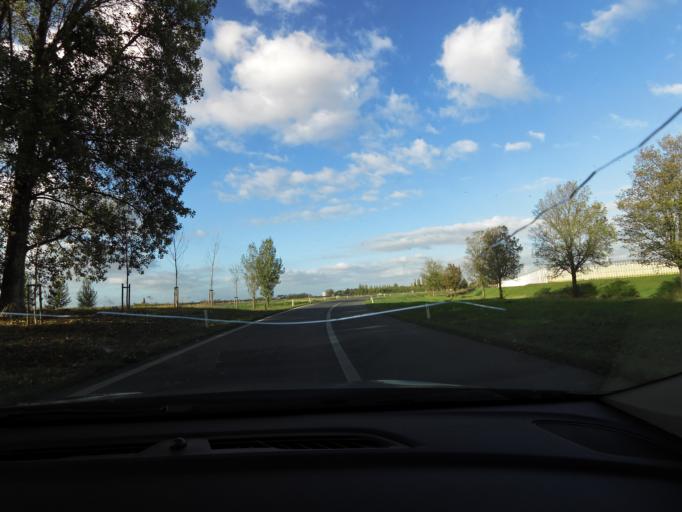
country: NL
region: North Brabant
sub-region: Gemeente Steenbergen
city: Dinteloord
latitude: 51.6260
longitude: 4.3837
